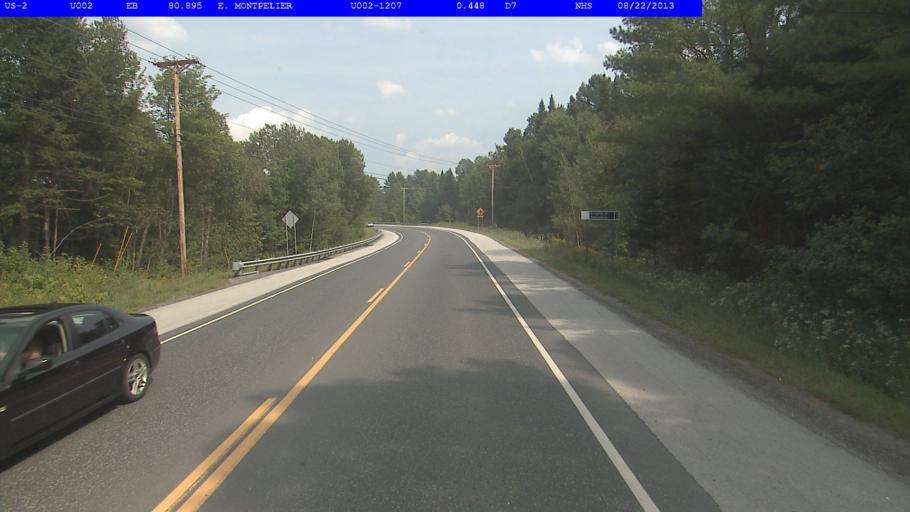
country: US
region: Vermont
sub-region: Washington County
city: Barre
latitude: 44.2424
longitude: -72.5090
